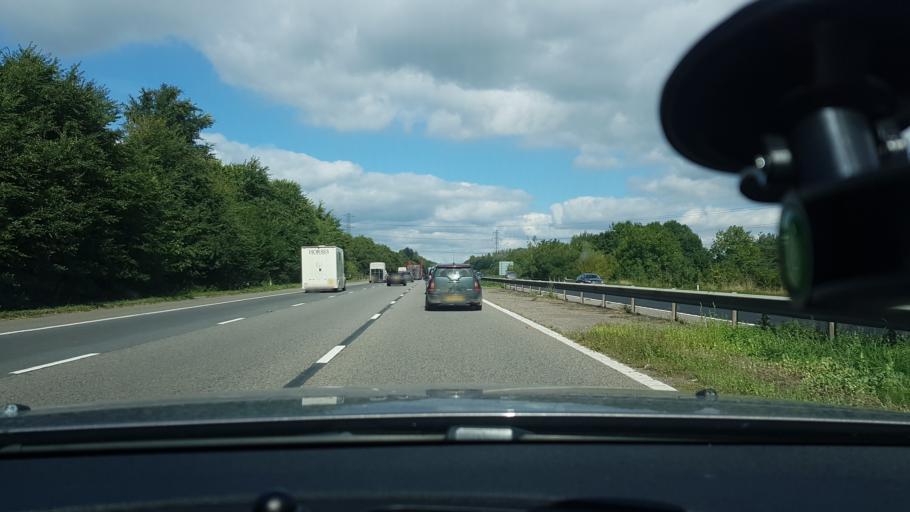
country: GB
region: England
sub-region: Devon
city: Cullompton
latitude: 50.8698
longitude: -3.3824
